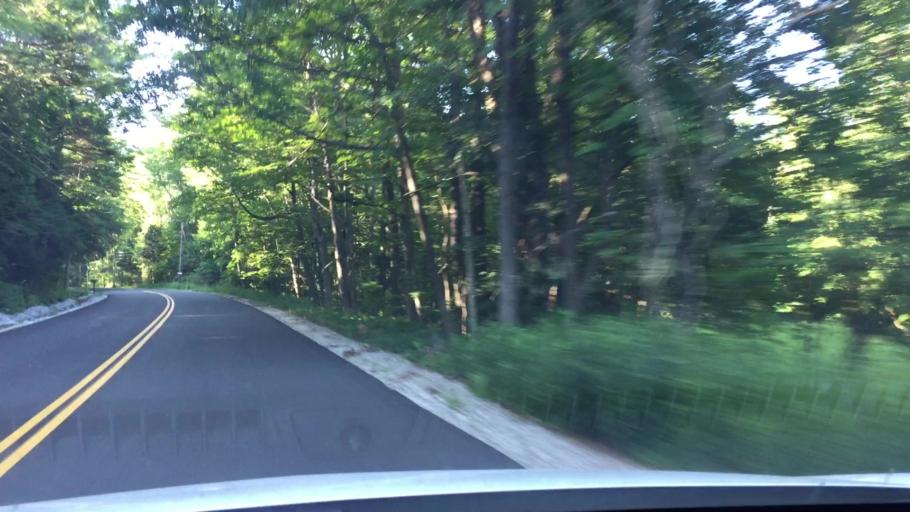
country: US
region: Massachusetts
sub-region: Berkshire County
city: Lee
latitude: 42.2863
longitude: -73.2144
